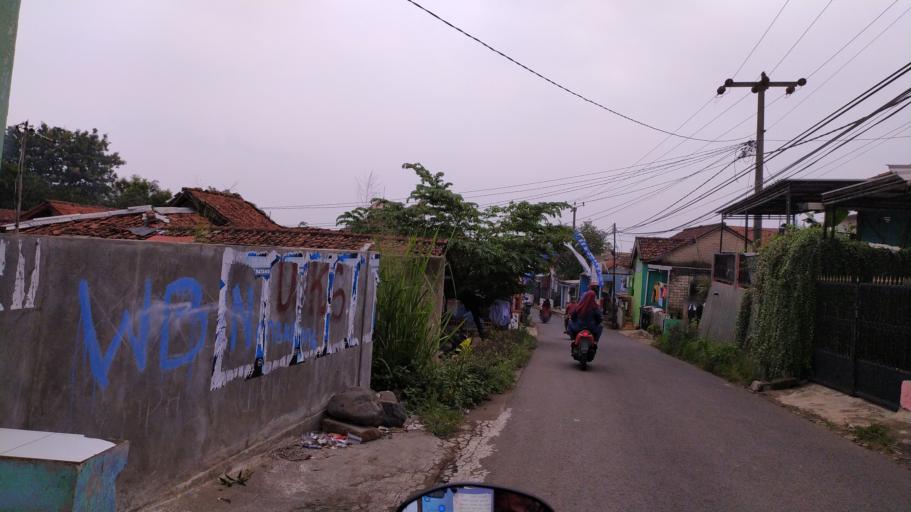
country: ID
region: West Java
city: Ciampea
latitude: -6.5870
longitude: 106.7056
